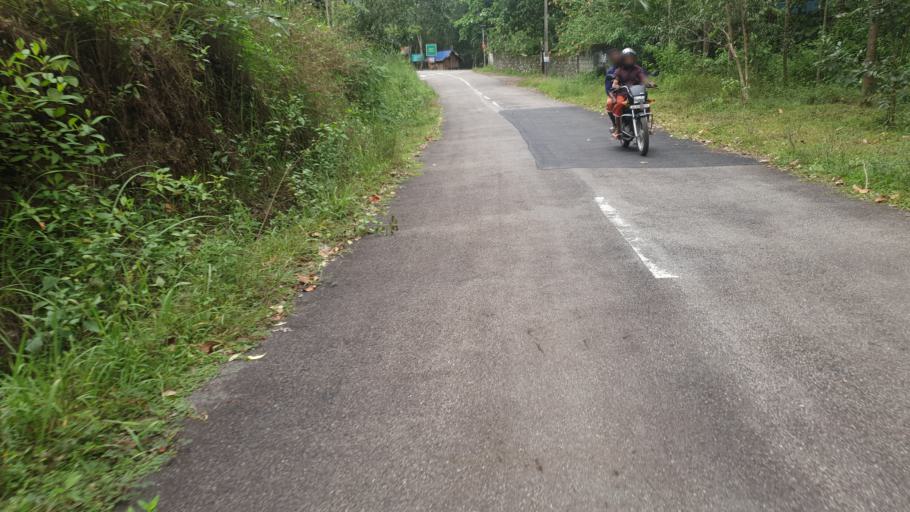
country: IN
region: Kerala
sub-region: Thiruvananthapuram
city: Nedumangad
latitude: 8.6347
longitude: 77.1119
